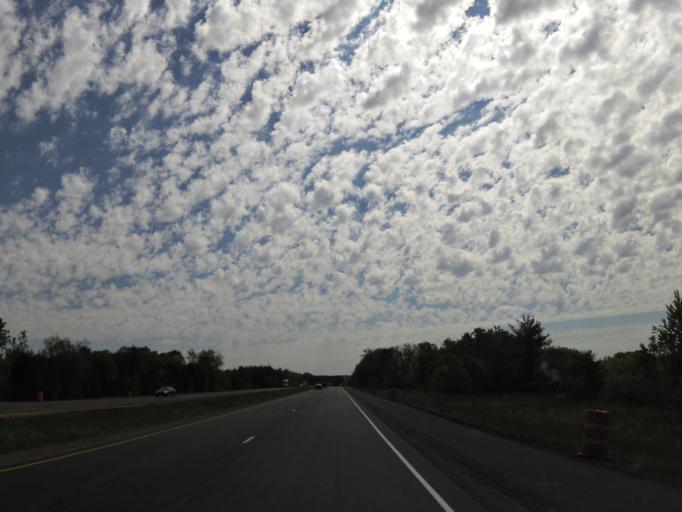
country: US
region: Wisconsin
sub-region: Dunn County
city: Colfax
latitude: 44.9019
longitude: -91.7757
